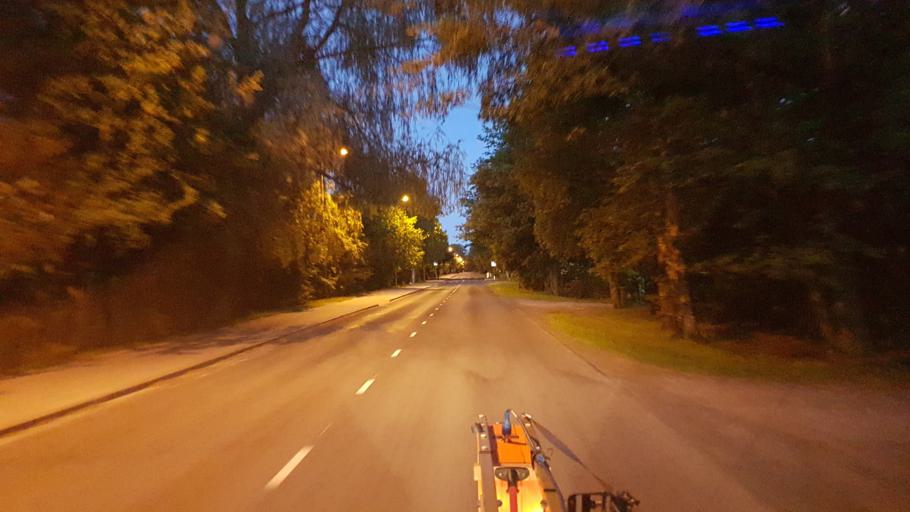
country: EE
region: Harju
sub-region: Harku vald
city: Tabasalu
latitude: 59.4404
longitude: 24.5967
